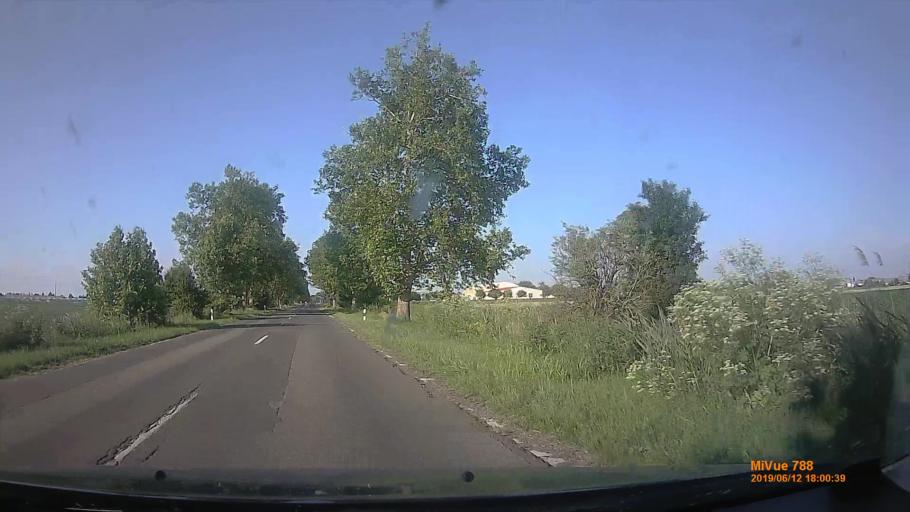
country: HU
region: Csongrad
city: Roszke
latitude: 46.2191
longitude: 20.0642
